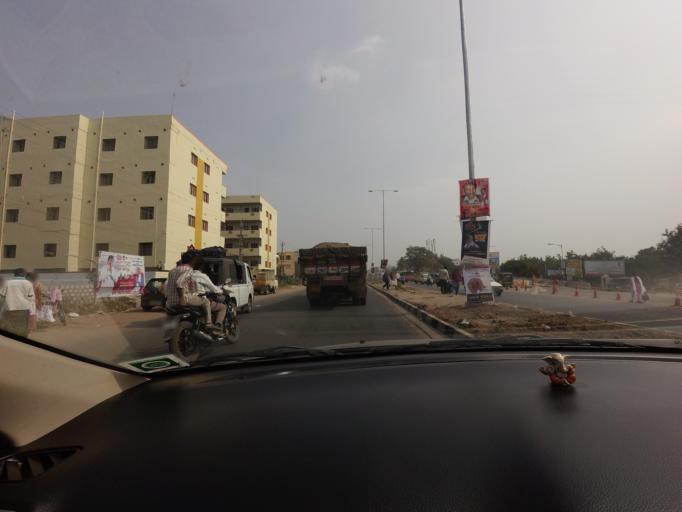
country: IN
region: Andhra Pradesh
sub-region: Krishna
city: Yanamalakuduru
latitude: 16.4795
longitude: 80.6986
